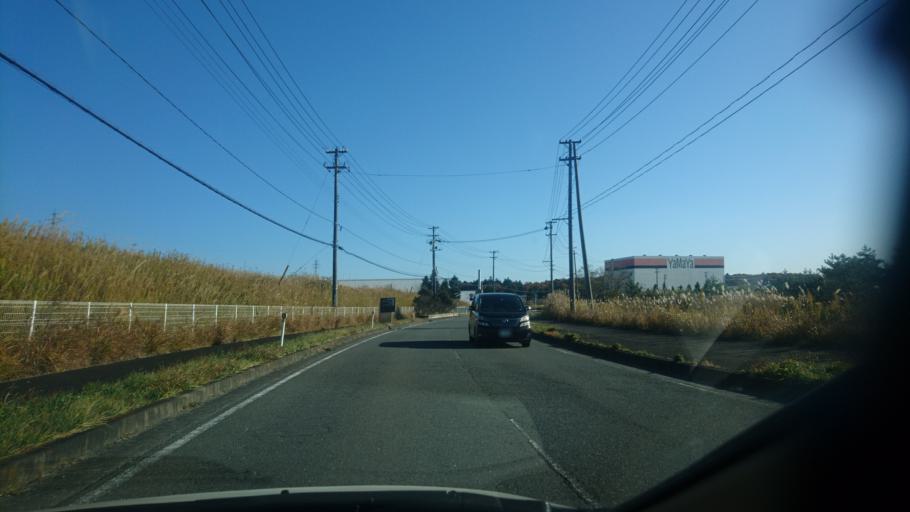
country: JP
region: Miyagi
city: Tomiya
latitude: 38.4601
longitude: 140.9358
